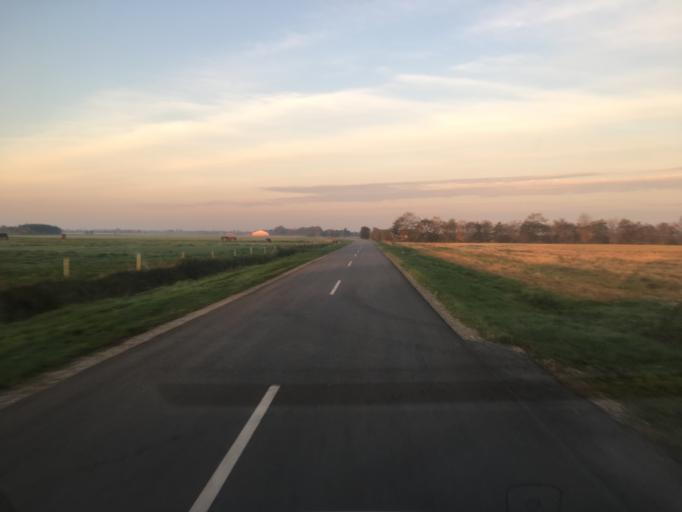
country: DK
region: South Denmark
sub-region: Tonder Kommune
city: Logumkloster
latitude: 55.0617
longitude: 9.0087
